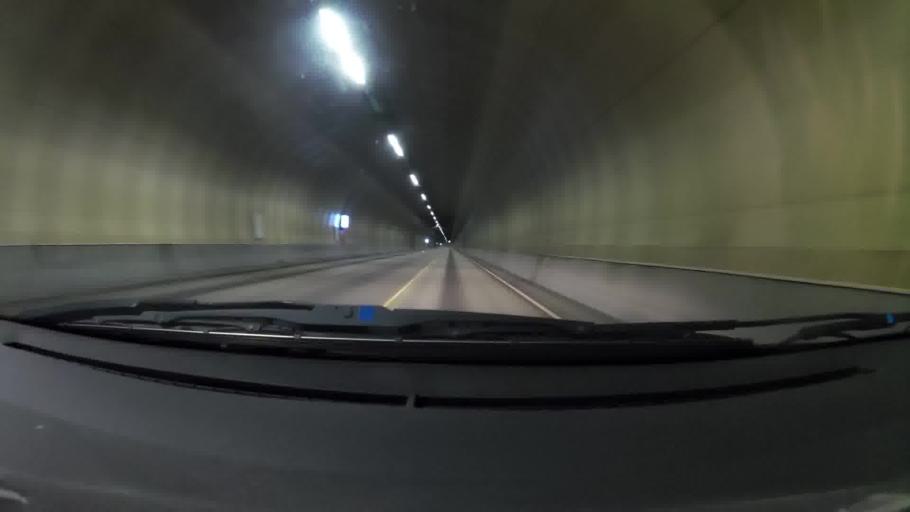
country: NO
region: More og Romsdal
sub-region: Kristiansund
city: Rensvik
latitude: 62.9828
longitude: 7.7965
